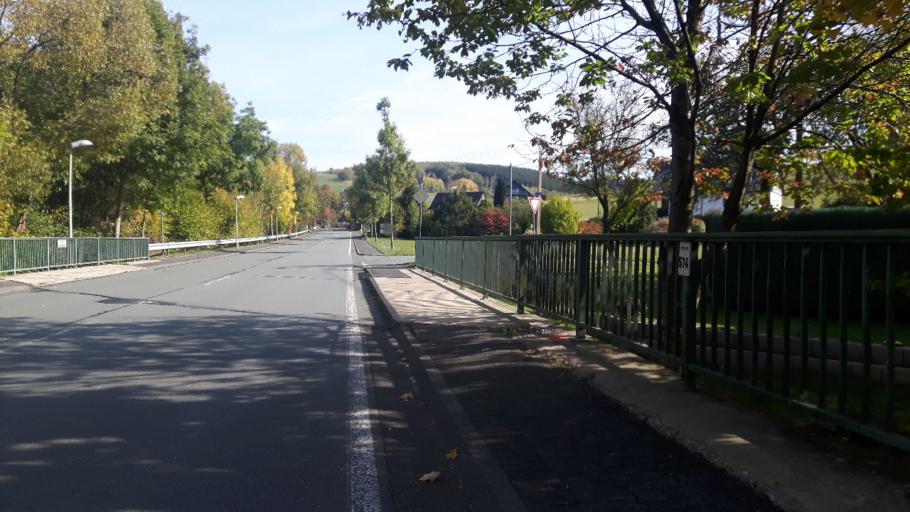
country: DE
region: North Rhine-Westphalia
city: Netphen
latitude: 50.8980
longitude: 8.1999
